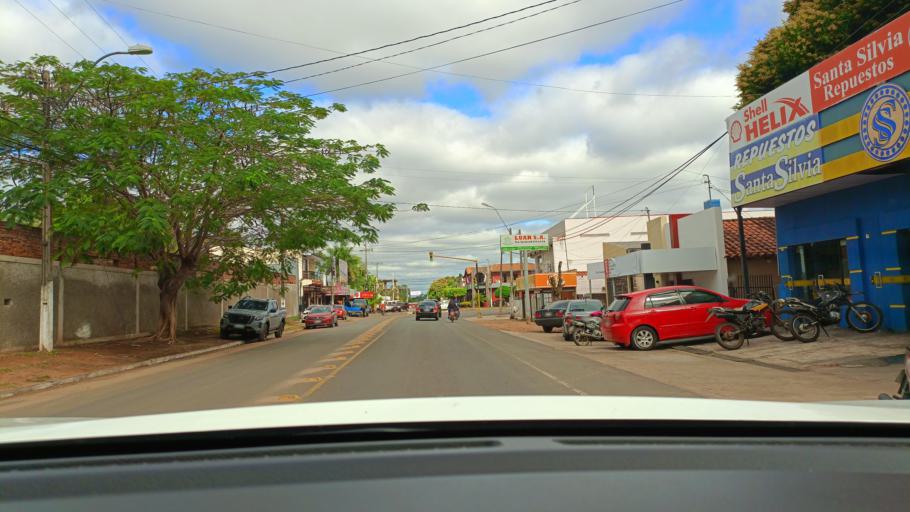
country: PY
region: San Pedro
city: Guayaybi
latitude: -24.6741
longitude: -56.4466
